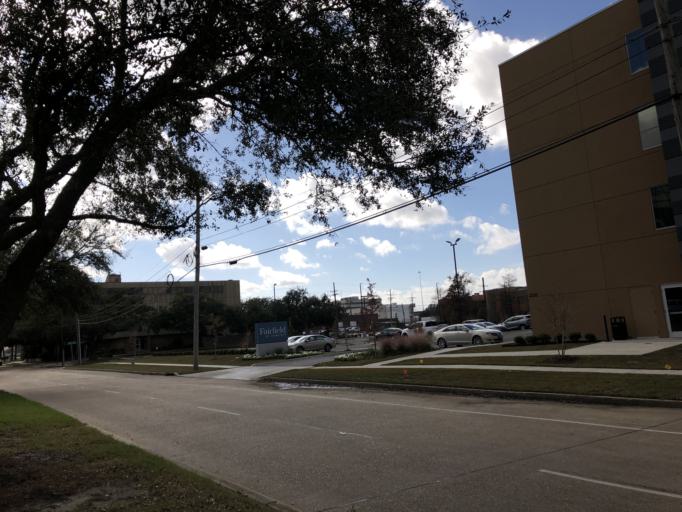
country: US
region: Louisiana
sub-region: Jefferson Parish
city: Metairie
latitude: 30.0006
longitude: -90.1595
